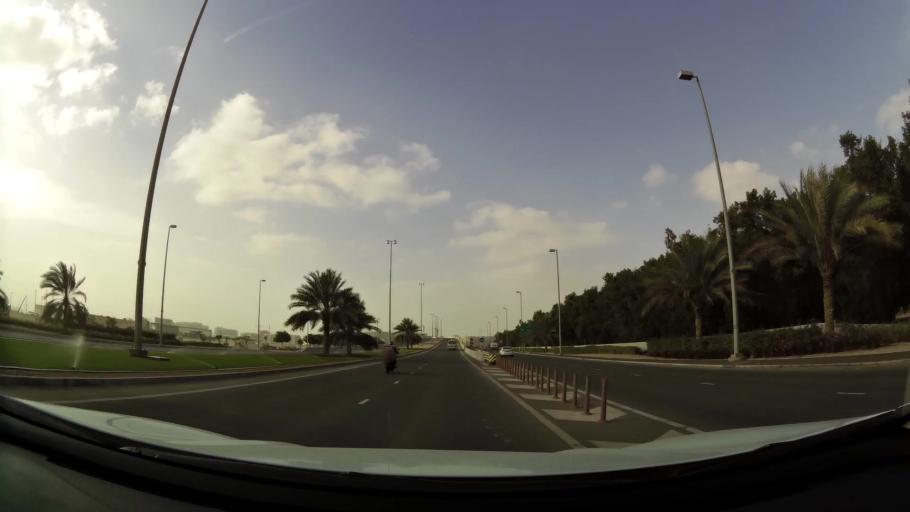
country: AE
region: Abu Dhabi
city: Abu Dhabi
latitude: 24.4435
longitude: 54.6201
